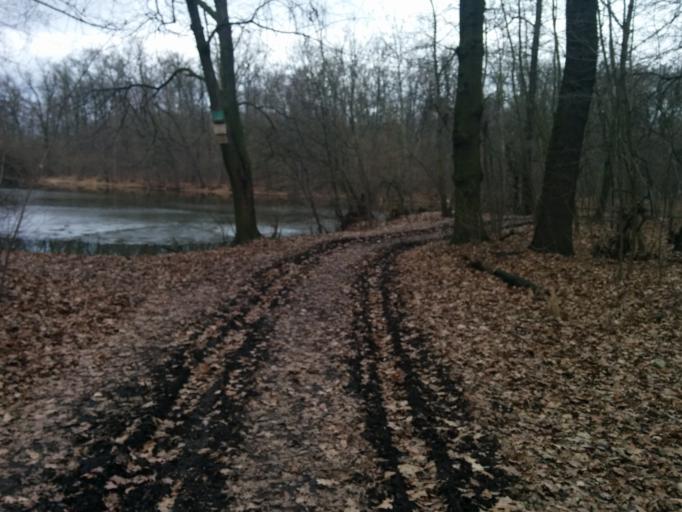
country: CZ
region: Central Bohemia
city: Libis
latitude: 50.2795
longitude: 14.5108
